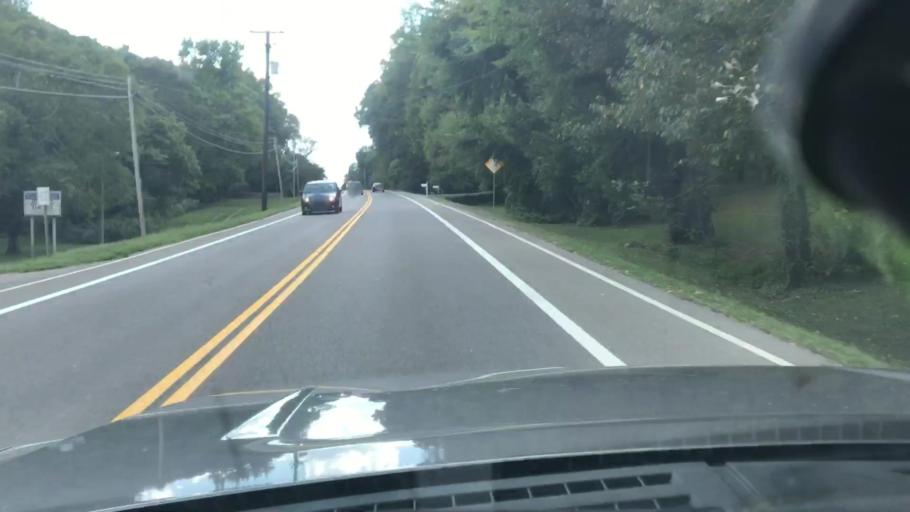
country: US
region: Tennessee
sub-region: Davidson County
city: Forest Hills
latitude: 36.0388
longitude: -86.8686
